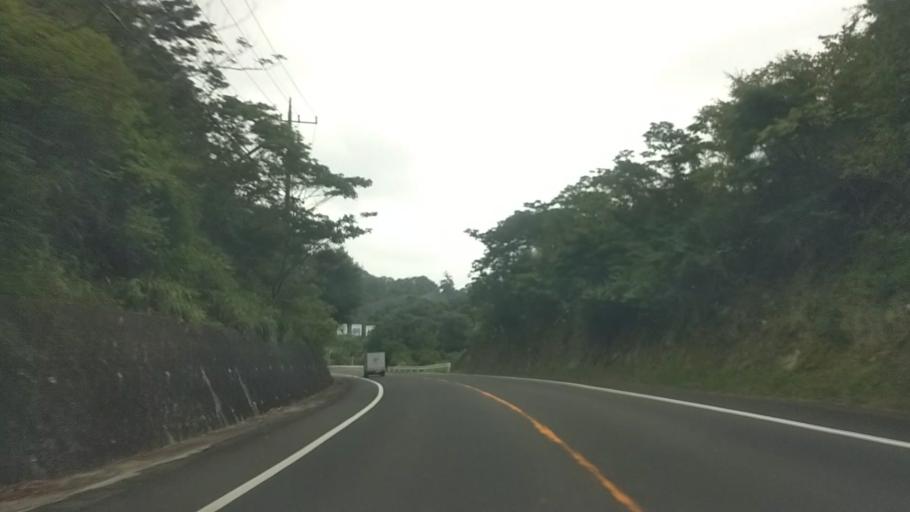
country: JP
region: Chiba
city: Kawaguchi
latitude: 35.1662
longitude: 140.0606
